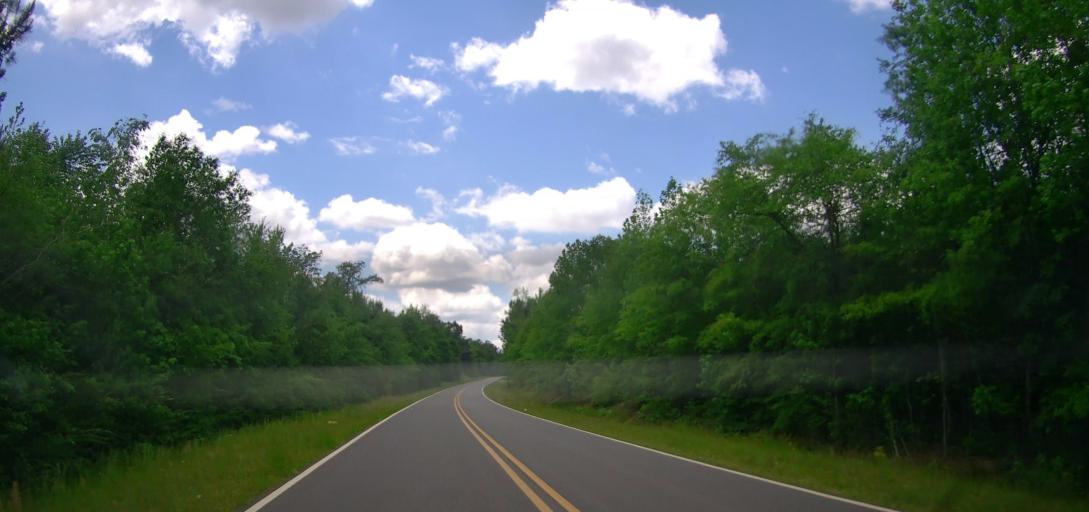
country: US
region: Georgia
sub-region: Laurens County
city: East Dublin
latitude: 32.6205
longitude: -82.8241
